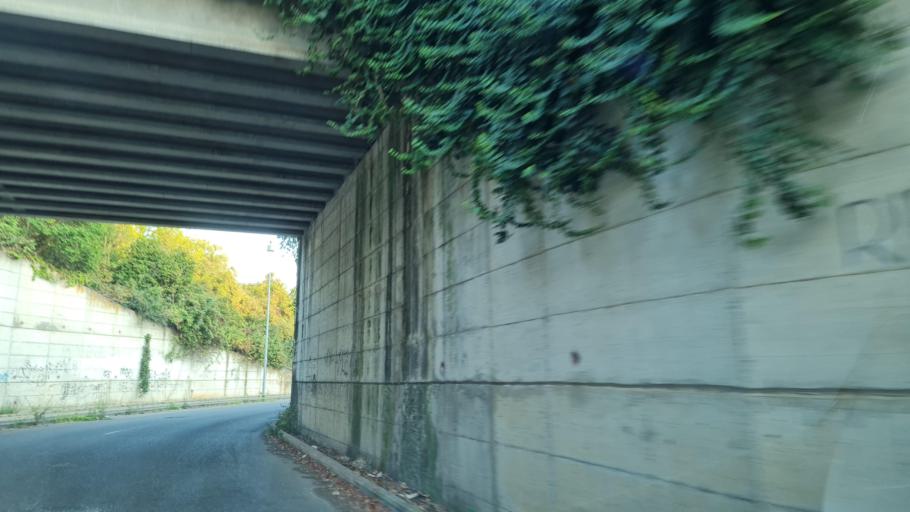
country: IT
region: Latium
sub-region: Provincia di Viterbo
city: Montalto di Castro
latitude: 42.3263
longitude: 11.6185
